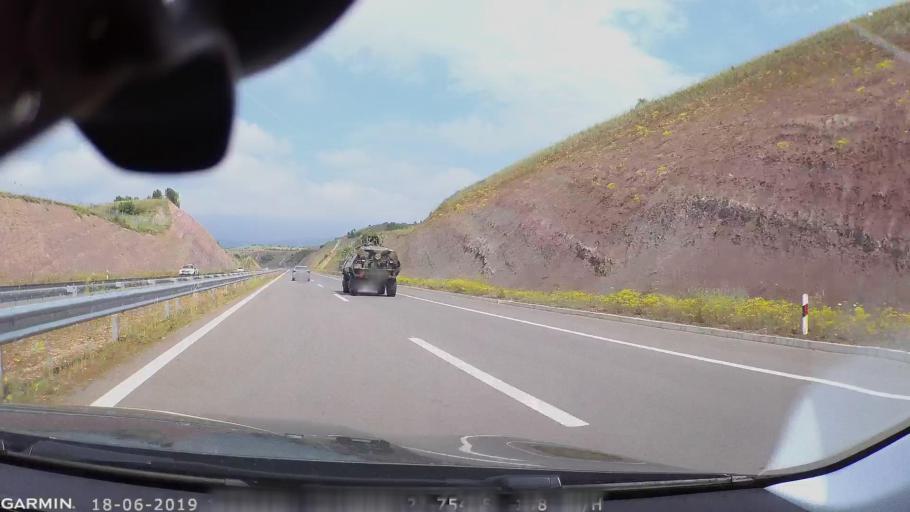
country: MK
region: Sveti Nikole
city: Gorobinci
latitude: 41.9251
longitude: 21.8382
